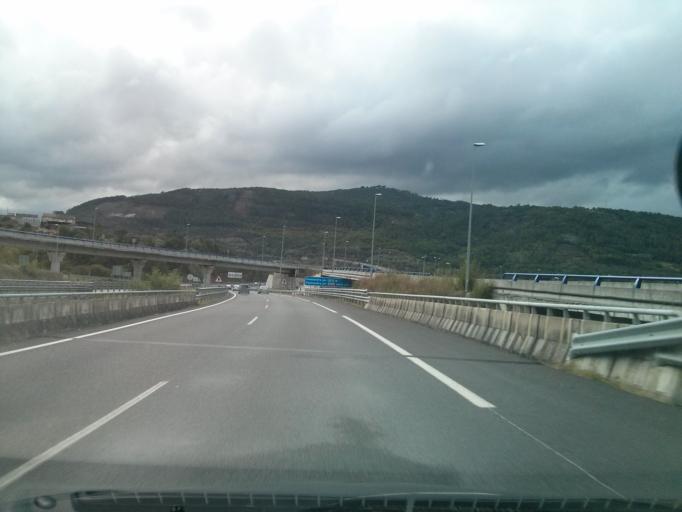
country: ES
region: Galicia
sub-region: Provincia de Ourense
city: Punxin
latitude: 42.3408
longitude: -7.9929
